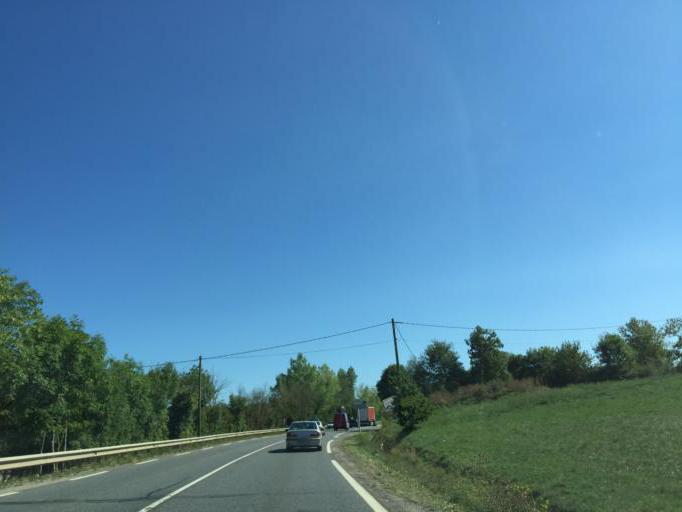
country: FR
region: Midi-Pyrenees
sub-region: Departement de l'Aveyron
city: Severac-le-Chateau
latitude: 44.3392
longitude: 3.0271
